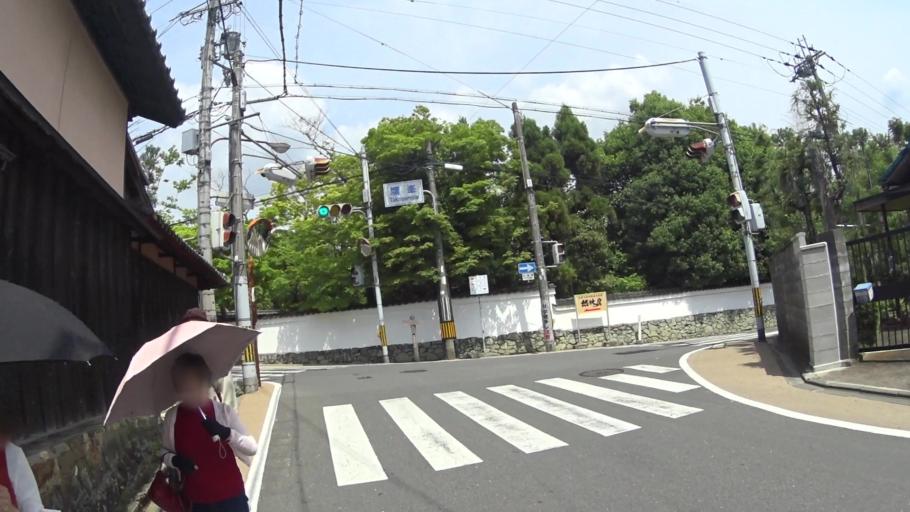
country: JP
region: Kyoto
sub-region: Kyoto-shi
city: Kamigyo-ku
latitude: 35.0540
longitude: 135.7321
